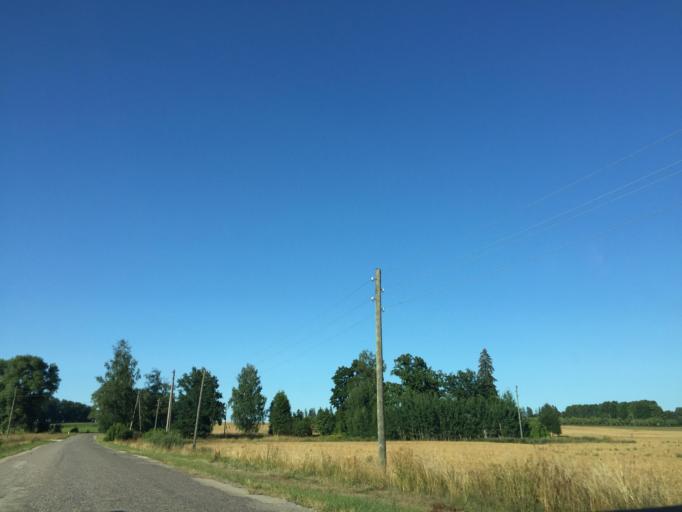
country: LV
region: Talsu Rajons
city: Stende
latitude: 57.1375
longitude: 22.6551
